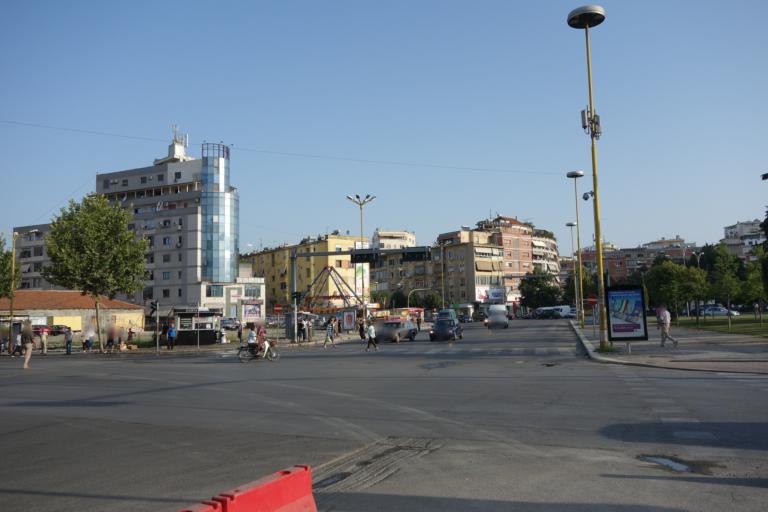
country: AL
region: Tirane
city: Tirana
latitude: 41.3280
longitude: 19.8163
